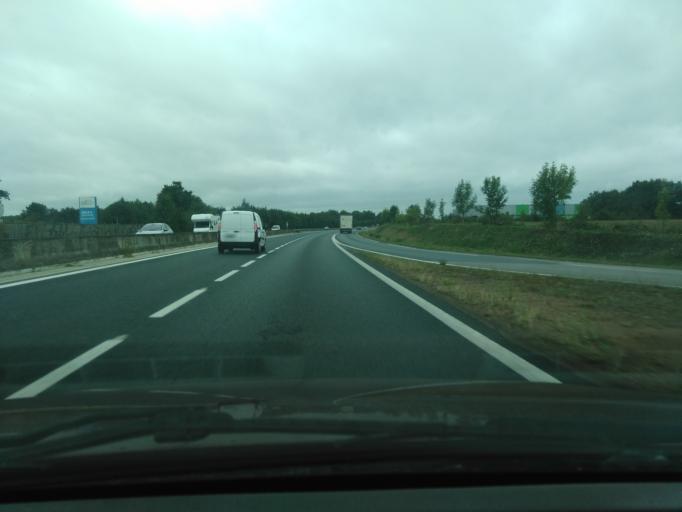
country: FR
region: Pays de la Loire
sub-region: Departement de la Vendee
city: La Chaize-le-Vicomte
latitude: 46.6667
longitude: -1.3455
